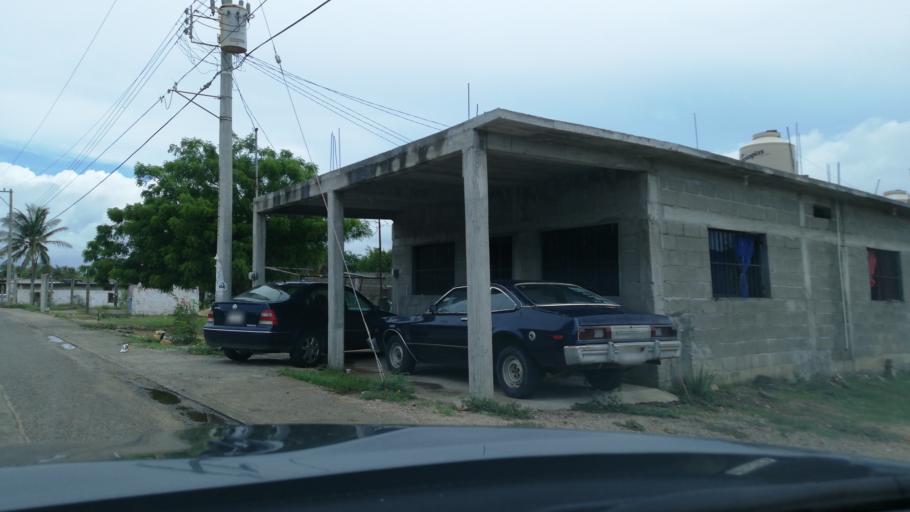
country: MX
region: Oaxaca
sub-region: Salina Cruz
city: Salina Cruz
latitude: 16.1636
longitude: -95.2190
